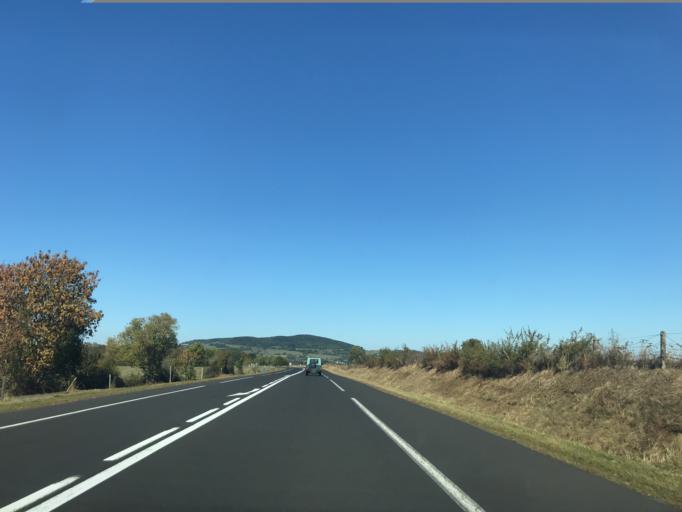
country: FR
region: Auvergne
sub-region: Departement du Puy-de-Dome
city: Gelles
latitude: 45.7095
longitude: 2.8103
